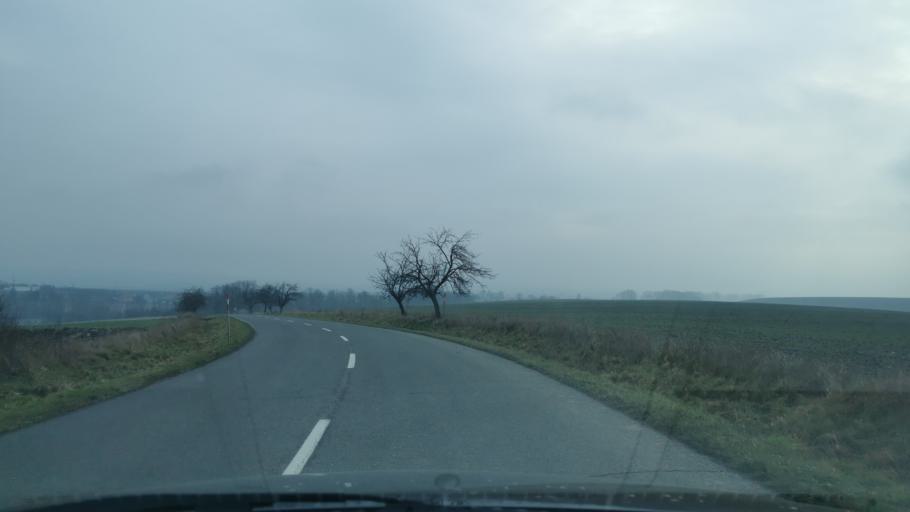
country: SK
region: Trnavsky
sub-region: Okres Senica
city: Senica
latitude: 48.7136
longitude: 17.3285
